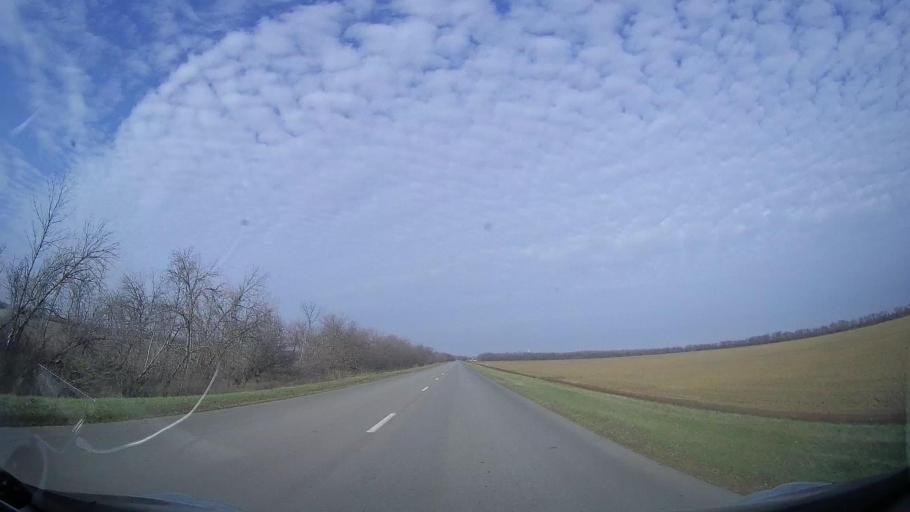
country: RU
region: Rostov
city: Gigant
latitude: 46.8249
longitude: 41.3392
